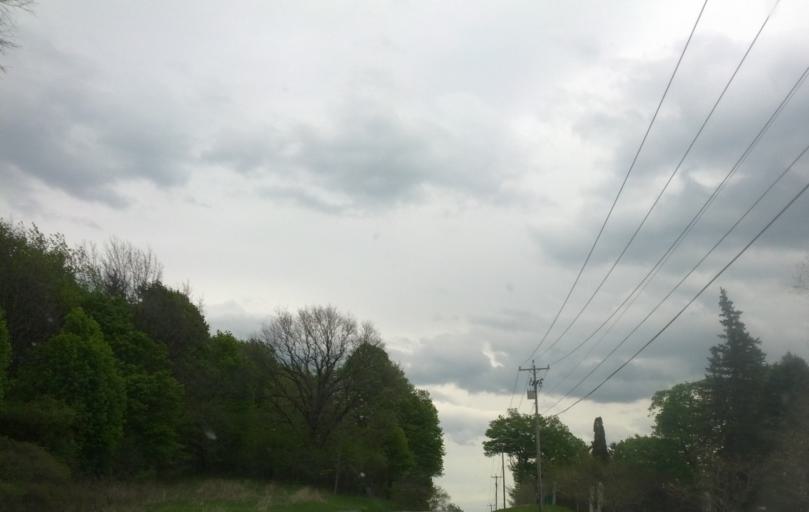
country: US
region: New York
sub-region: Onondaga County
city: Fayetteville
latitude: 42.9910
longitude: -76.0574
